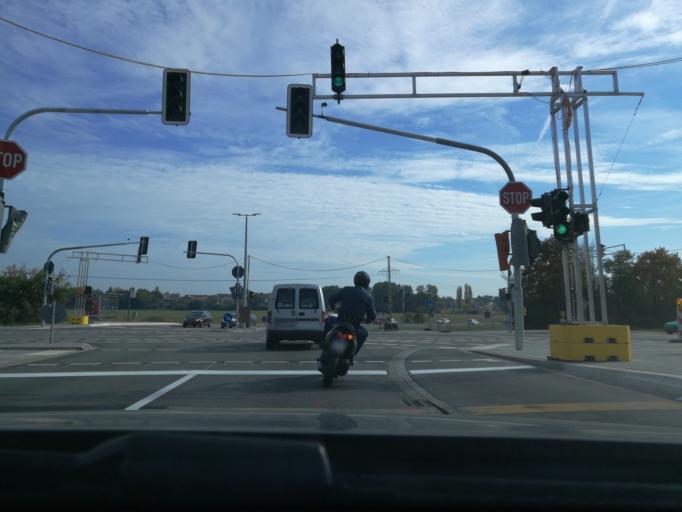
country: DE
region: Bavaria
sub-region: Regierungsbezirk Mittelfranken
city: Furth
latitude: 49.5121
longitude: 10.9639
